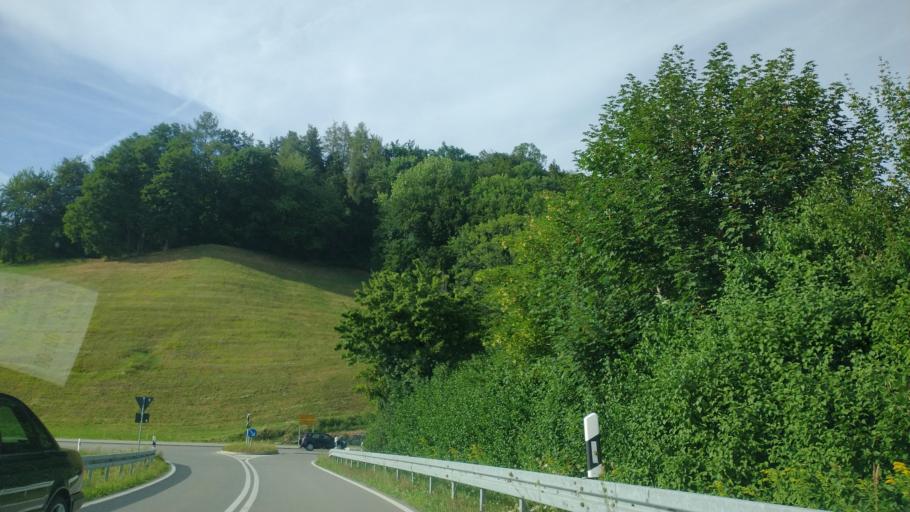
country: DE
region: Baden-Wuerttemberg
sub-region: Tuebingen Region
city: Kressbronn am Bodensee
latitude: 47.6305
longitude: 9.5933
